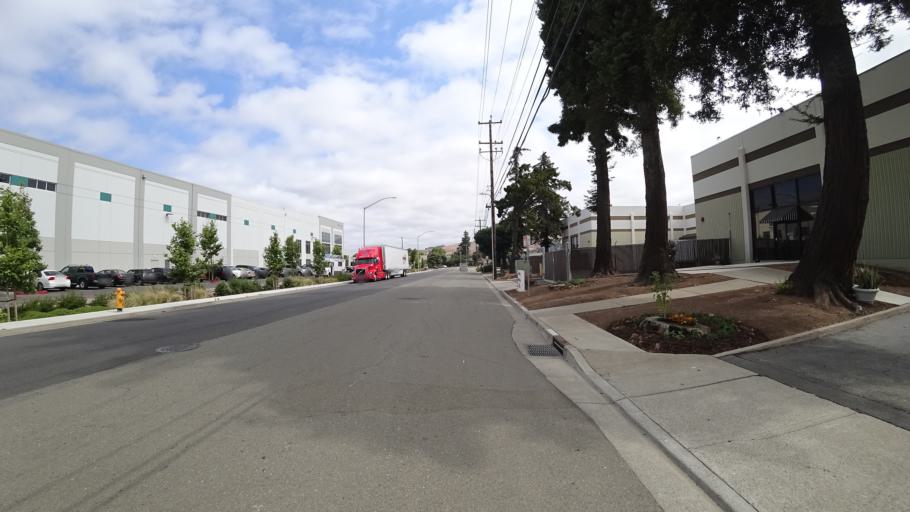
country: US
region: California
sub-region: Alameda County
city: Union City
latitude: 37.6102
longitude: -122.0450
